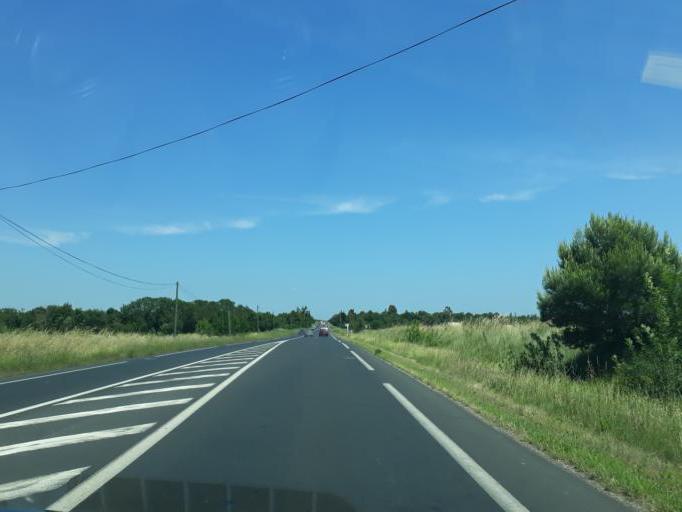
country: FR
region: Languedoc-Roussillon
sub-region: Departement de l'Herault
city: Portiragnes
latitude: 43.3137
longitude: 3.3473
